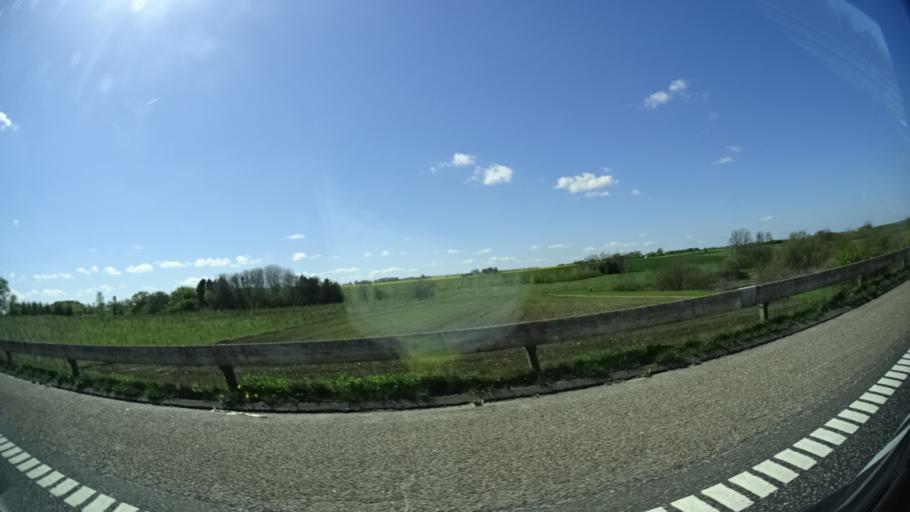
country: DK
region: Central Jutland
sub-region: Favrskov Kommune
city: Hadsten
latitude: 56.3431
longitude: 10.1204
